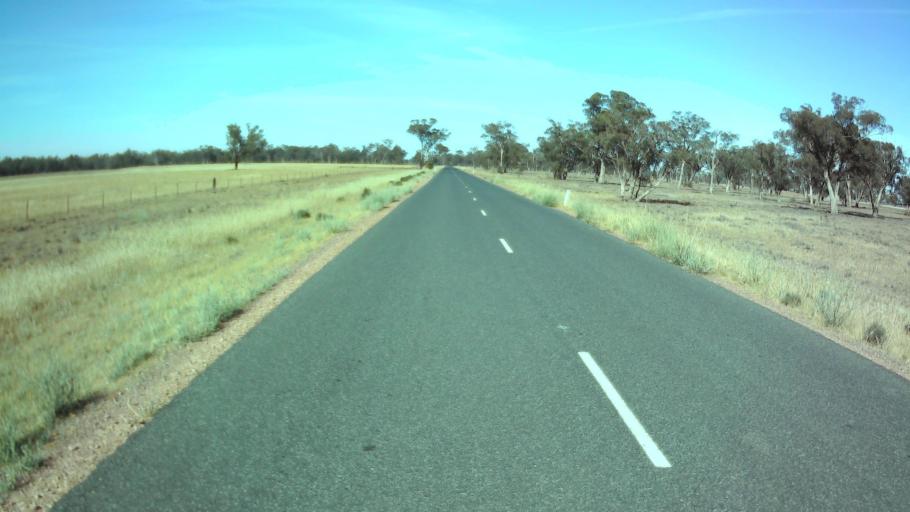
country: AU
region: New South Wales
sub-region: Weddin
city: Grenfell
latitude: -34.1085
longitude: 147.8575
